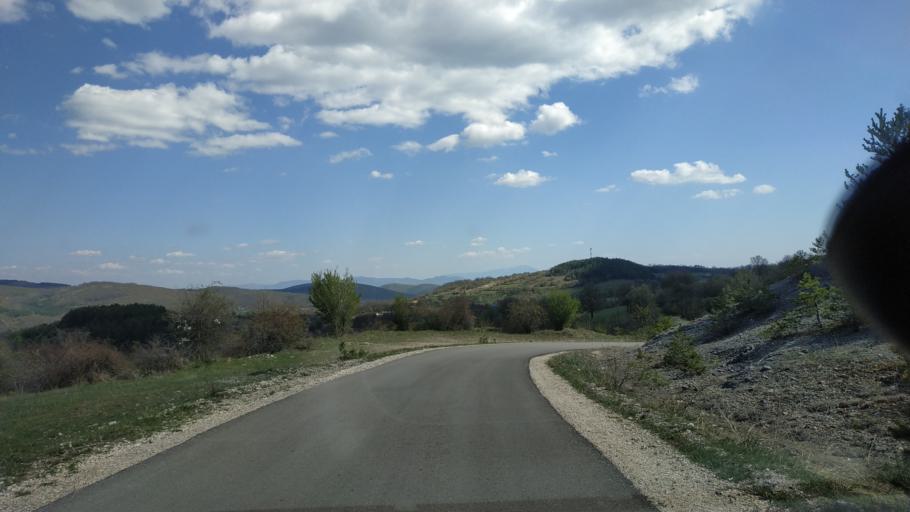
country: RS
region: Central Serbia
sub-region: Zajecarski Okrug
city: Soko Banja
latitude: 43.5768
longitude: 21.8946
